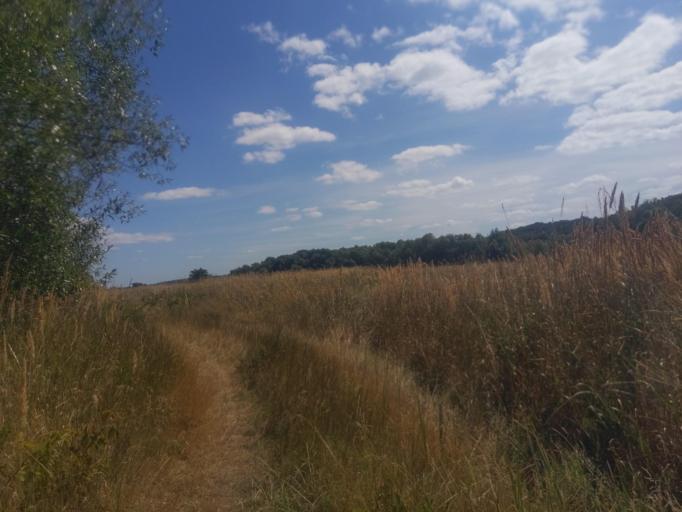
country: DE
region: Lower Saxony
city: Tosterglope
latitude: 53.2562
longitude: 10.8228
